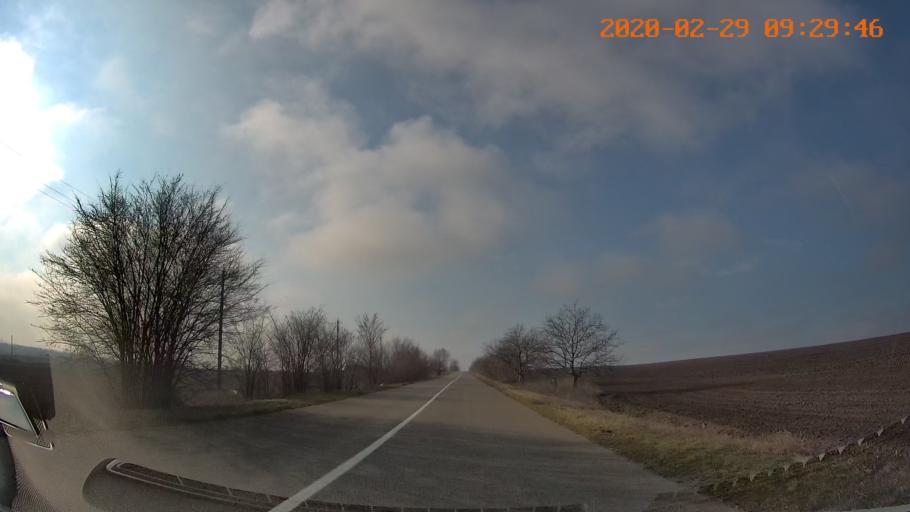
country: UA
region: Odessa
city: Lymanske
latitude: 46.6746
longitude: 29.9196
